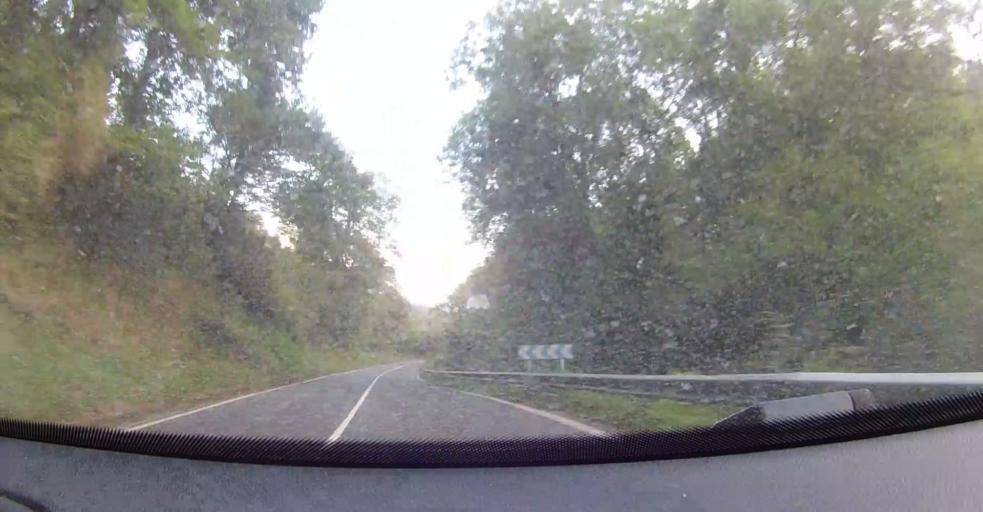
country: ES
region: Basque Country
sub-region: Bizkaia
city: Urrestieta
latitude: 43.2371
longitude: -3.1585
